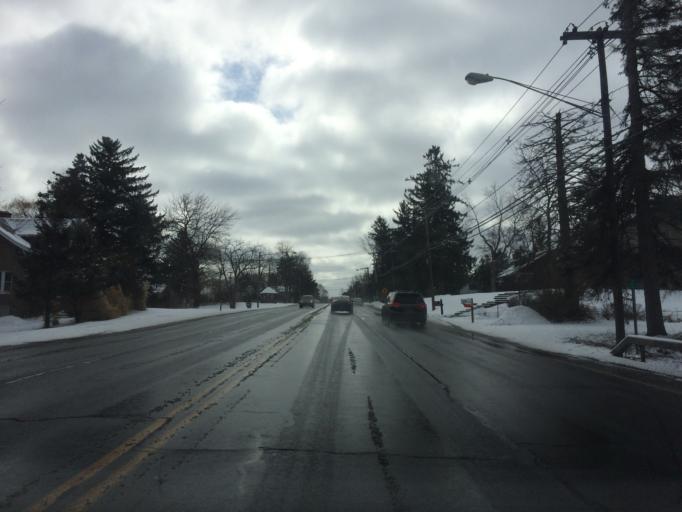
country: US
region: New York
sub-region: Monroe County
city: Pittsford
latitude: 43.0992
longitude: -77.5335
